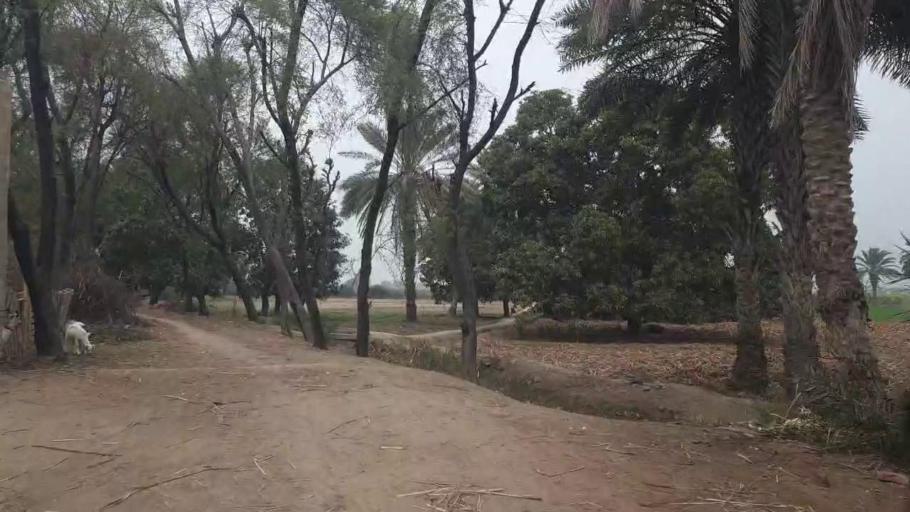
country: PK
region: Sindh
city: Shahdadpur
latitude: 25.8625
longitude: 68.6475
